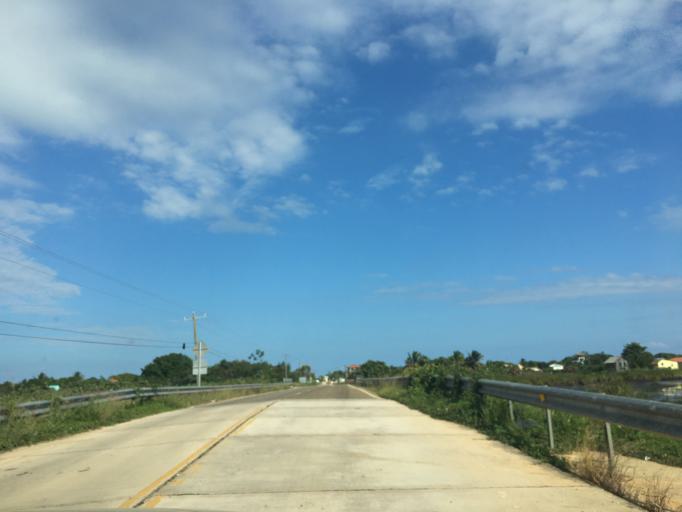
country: BZ
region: Stann Creek
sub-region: Dangriga
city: Dangriga
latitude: 16.8620
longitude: -88.2893
